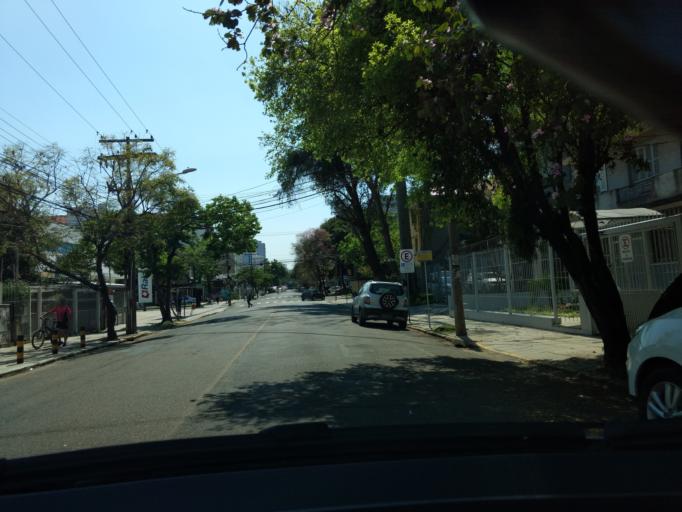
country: BR
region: Rio Grande do Sul
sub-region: Porto Alegre
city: Porto Alegre
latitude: -30.0426
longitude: -51.2118
